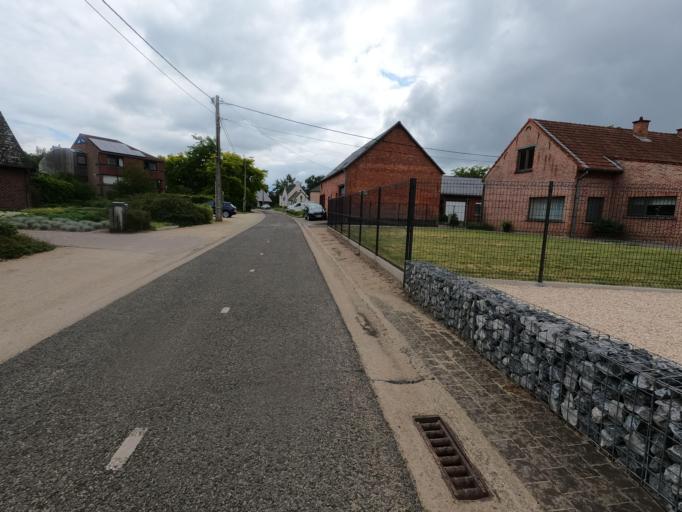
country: BE
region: Flanders
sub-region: Provincie Vlaams-Brabant
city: Tremelo
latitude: 50.9765
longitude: 4.7161
